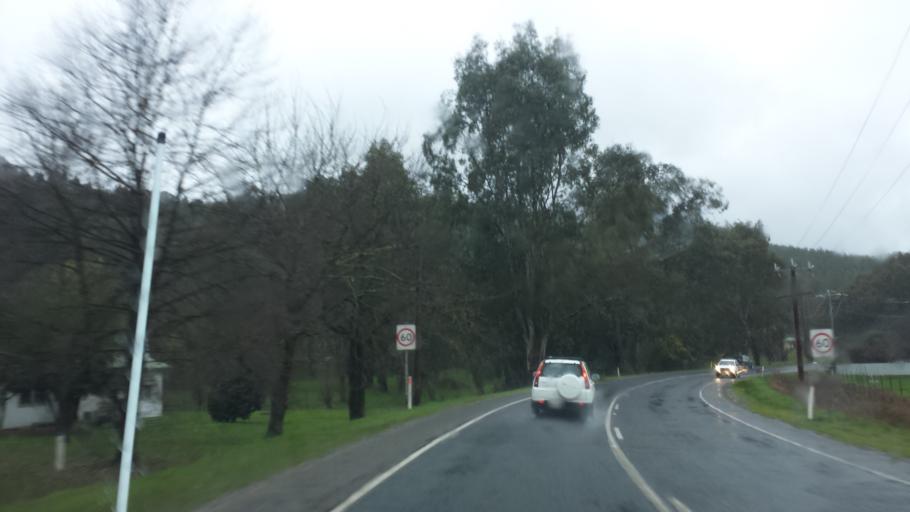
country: AU
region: Victoria
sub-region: Wangaratta
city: Wangaratta
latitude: -36.5699
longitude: 146.7351
